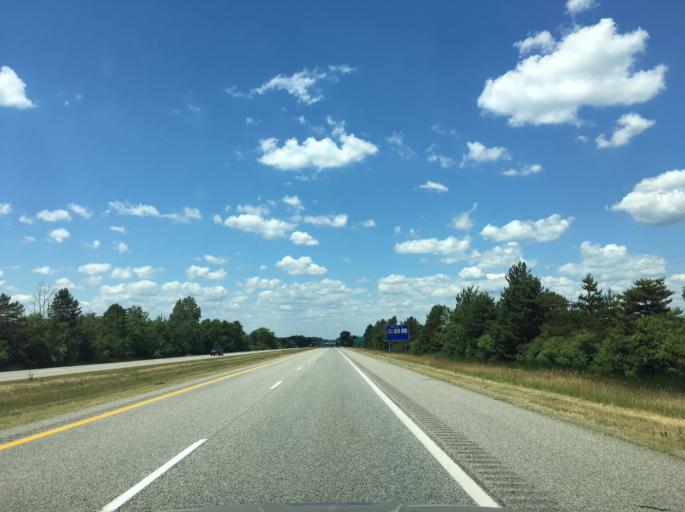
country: US
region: Michigan
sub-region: Midland County
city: Midland
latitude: 43.6559
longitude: -84.2146
